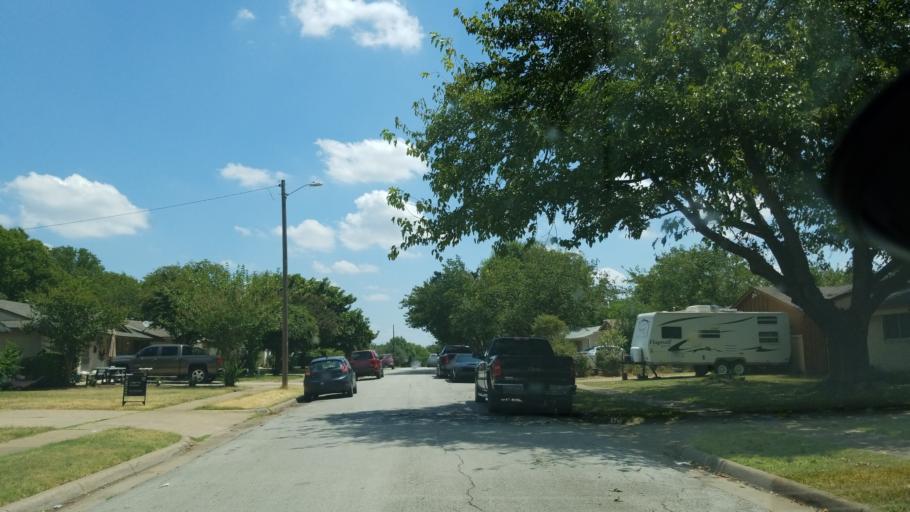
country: US
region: Texas
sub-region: Dallas County
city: Duncanville
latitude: 32.6650
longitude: -96.8970
